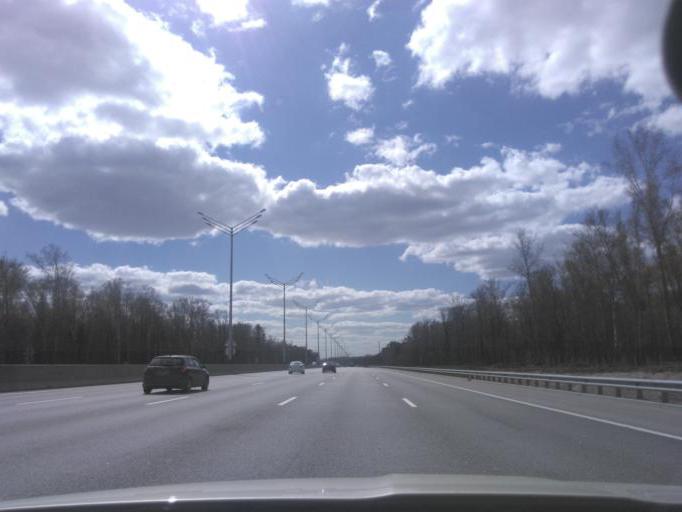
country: RU
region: Moscow
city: Khimki
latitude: 55.9292
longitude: 37.4528
